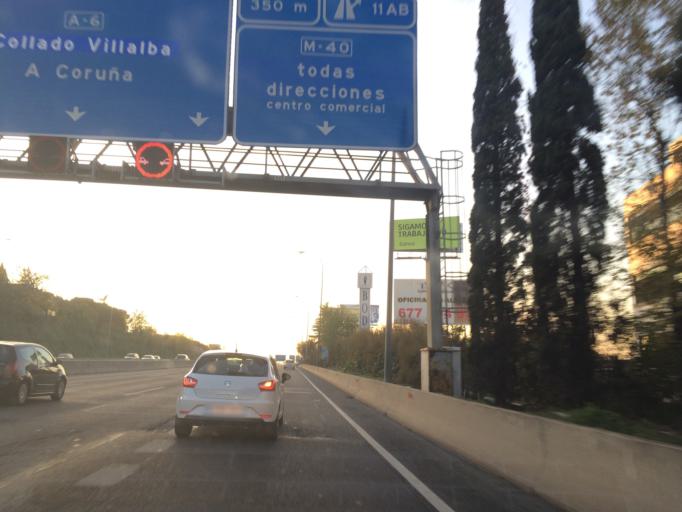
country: ES
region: Madrid
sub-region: Provincia de Madrid
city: Pozuelo de Alarcon
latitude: 40.4641
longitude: -3.7863
